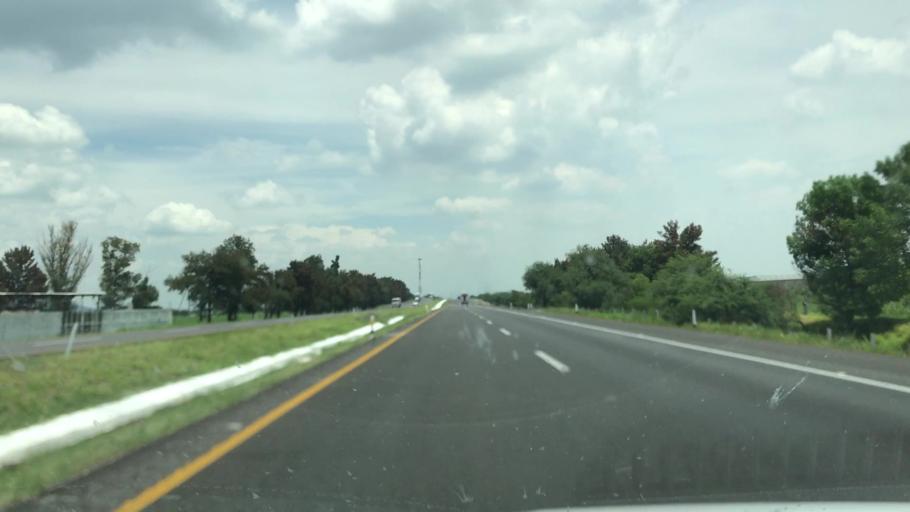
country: MX
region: Guanajuato
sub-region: Salamanca
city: San Vicente de Flores
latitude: 20.6243
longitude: -101.2403
